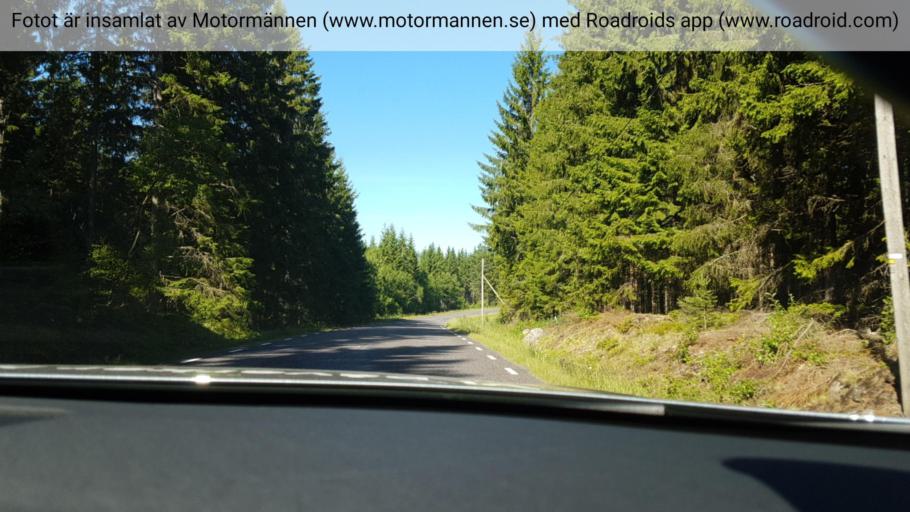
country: SE
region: Vaestra Goetaland
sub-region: Ulricehamns Kommun
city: Ulricehamn
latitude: 57.8383
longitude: 13.3397
